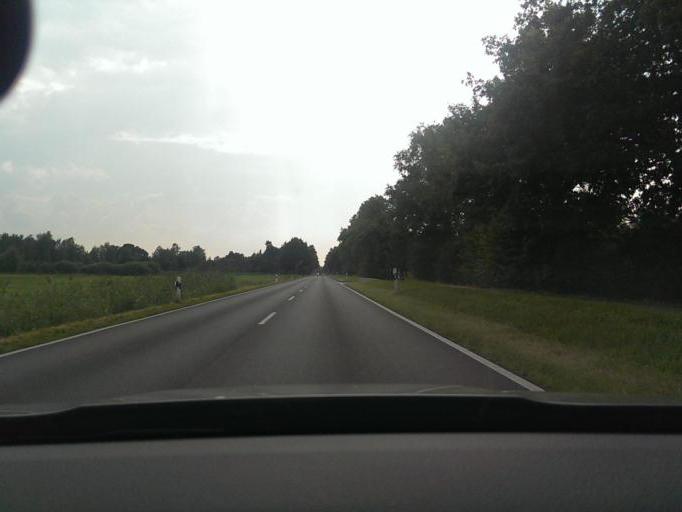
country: DE
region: Lower Saxony
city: Worpswede
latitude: 53.2135
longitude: 8.8979
